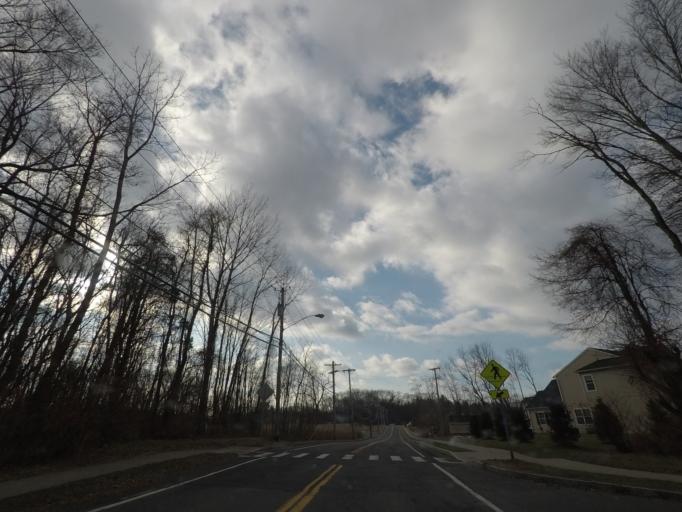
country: US
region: New York
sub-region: Albany County
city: McKownville
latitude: 42.6646
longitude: -73.8407
